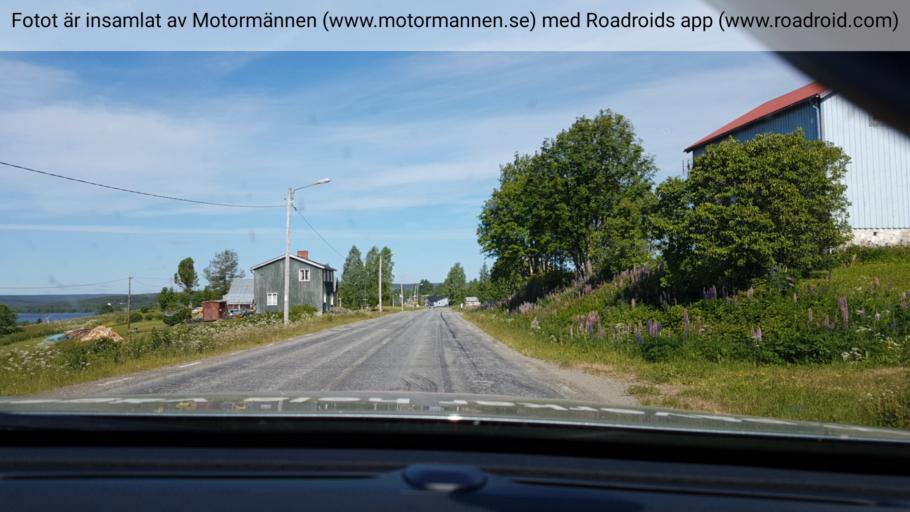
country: SE
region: Vaesterbotten
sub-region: Dorotea Kommun
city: Dorotea
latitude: 64.4161
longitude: 16.0150
